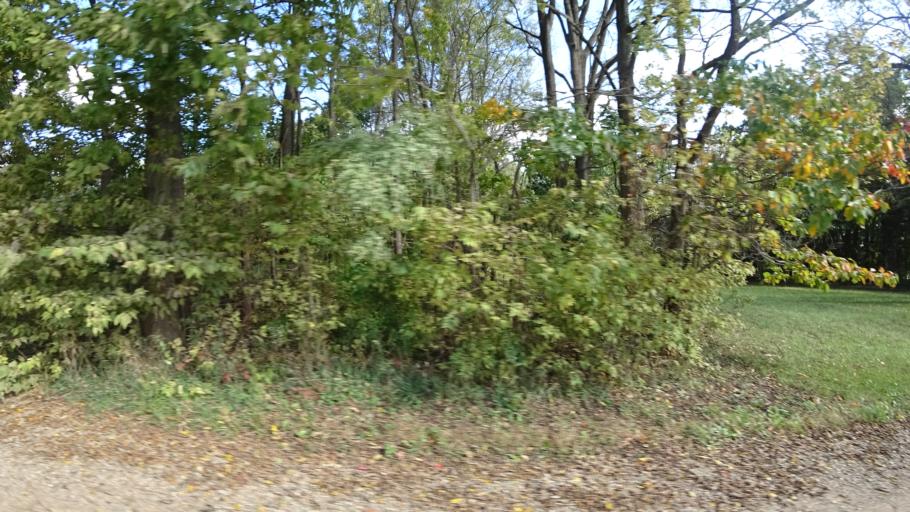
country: US
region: Michigan
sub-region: Saint Joseph County
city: Three Rivers
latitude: 41.9465
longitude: -85.6152
